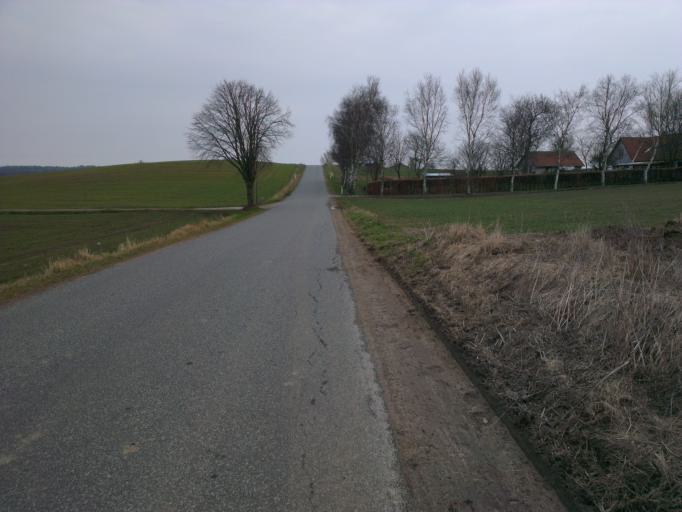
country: DK
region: Capital Region
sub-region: Frederikssund Kommune
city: Skibby
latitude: 55.7442
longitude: 11.9006
